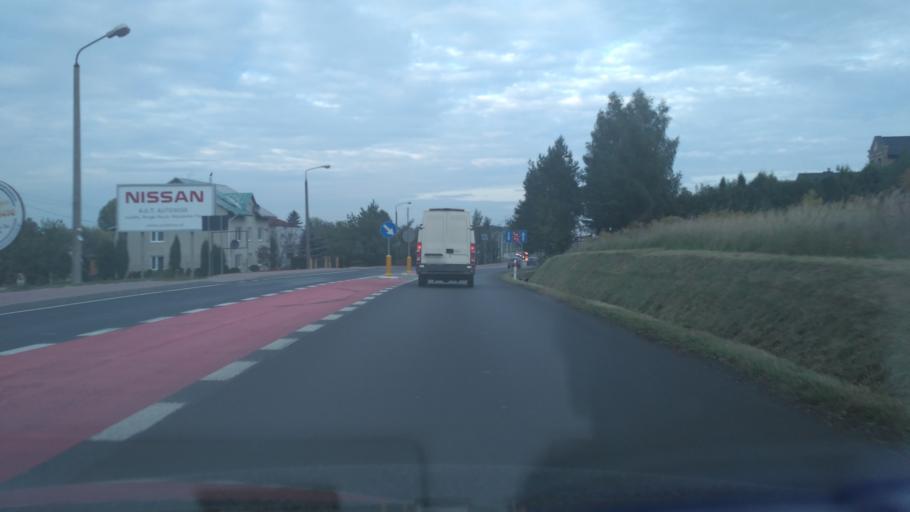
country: PL
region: Lublin Voivodeship
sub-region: Powiat lubelski
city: Jakubowice Murowane
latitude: 51.2722
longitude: 22.6423
